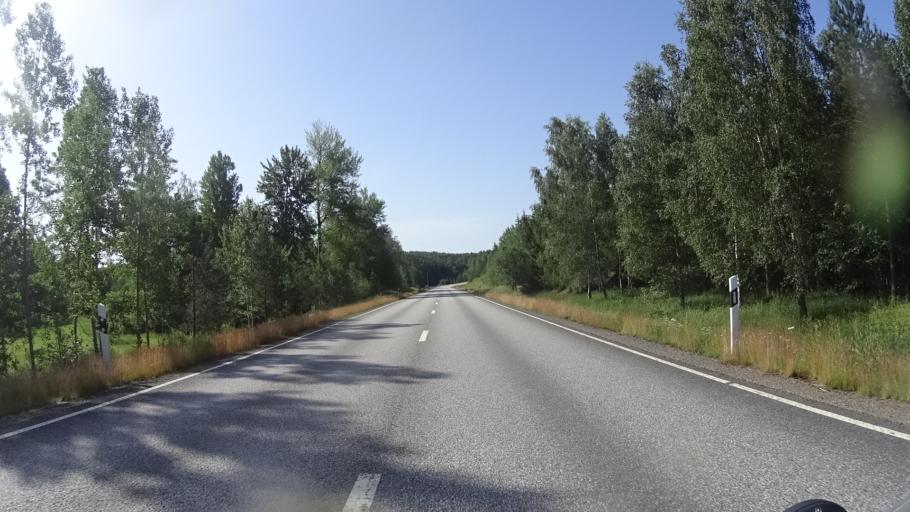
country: SE
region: Kalmar
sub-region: Vasterviks Kommun
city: Overum
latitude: 58.0632
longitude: 16.2036
